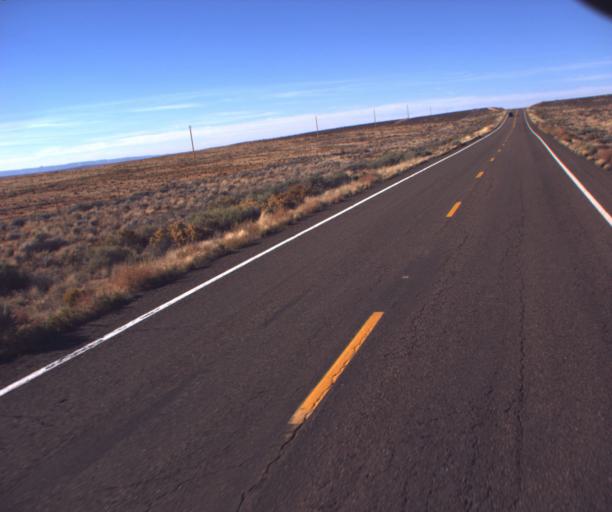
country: US
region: Arizona
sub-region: Coconino County
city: LeChee
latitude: 36.7200
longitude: -111.2765
